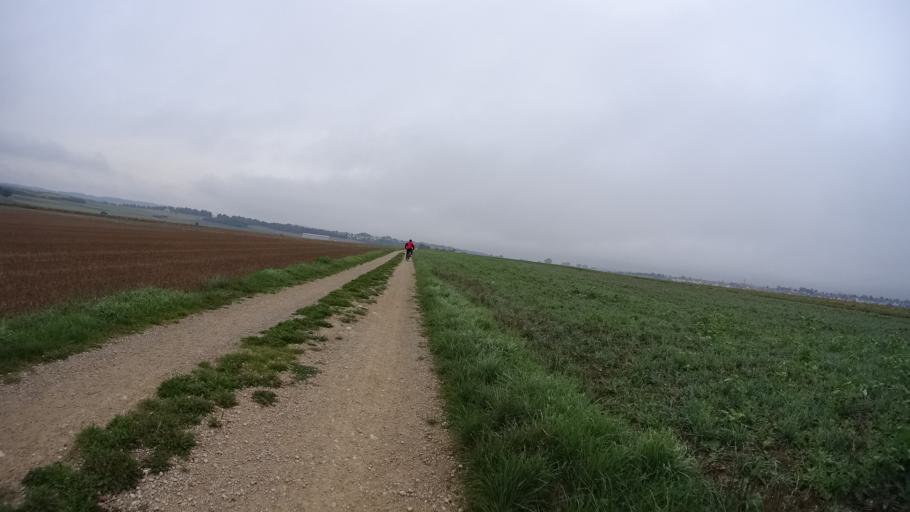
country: DE
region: Bavaria
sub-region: Upper Bavaria
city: Gaimersheim
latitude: 48.8163
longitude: 11.3897
